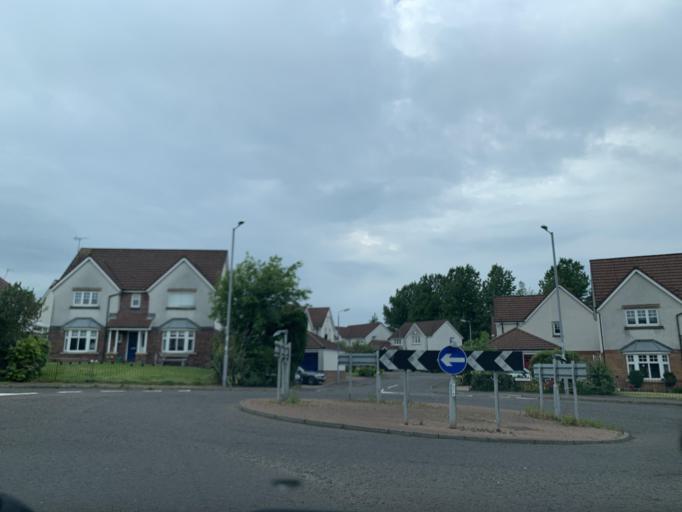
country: GB
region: Scotland
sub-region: East Renfrewshire
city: Newton Mearns
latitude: 55.7734
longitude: -4.3498
